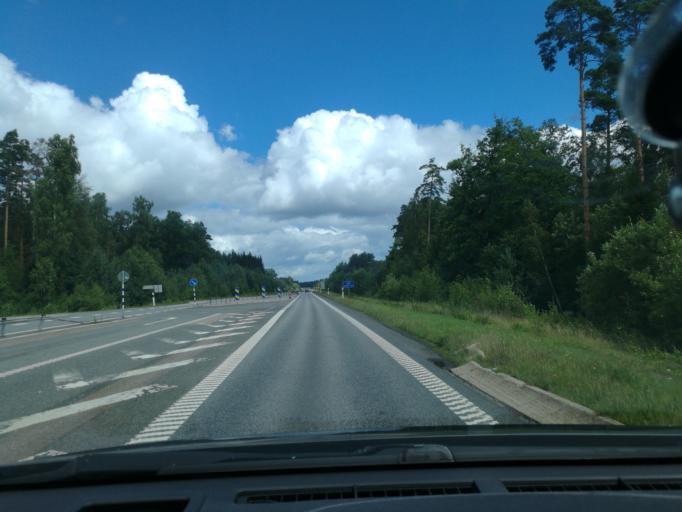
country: SE
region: Skane
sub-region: Hassleholms Kommun
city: Hassleholm
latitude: 56.1989
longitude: 13.8558
